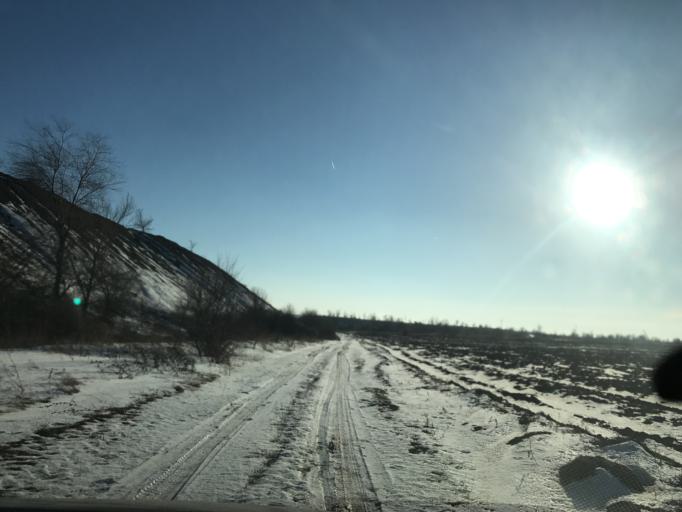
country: RU
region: Rostov
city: Staraya Stanitsa
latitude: 48.2381
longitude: 40.3944
